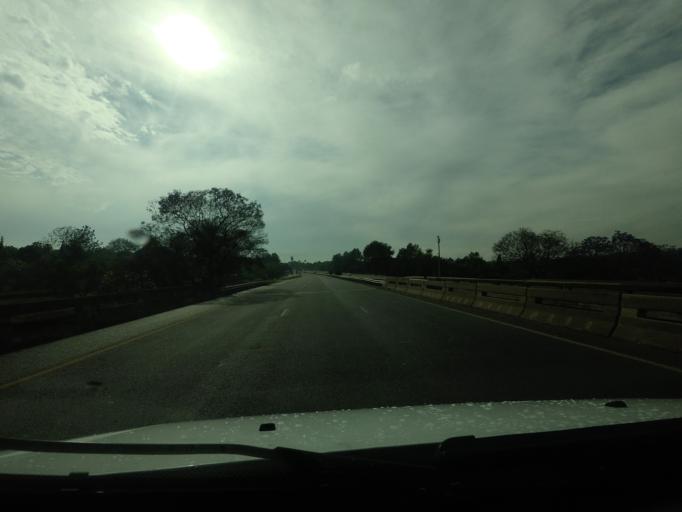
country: ZA
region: Gauteng
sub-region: City of Tshwane Metropolitan Municipality
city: Pretoria
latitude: -25.7530
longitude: 28.3046
